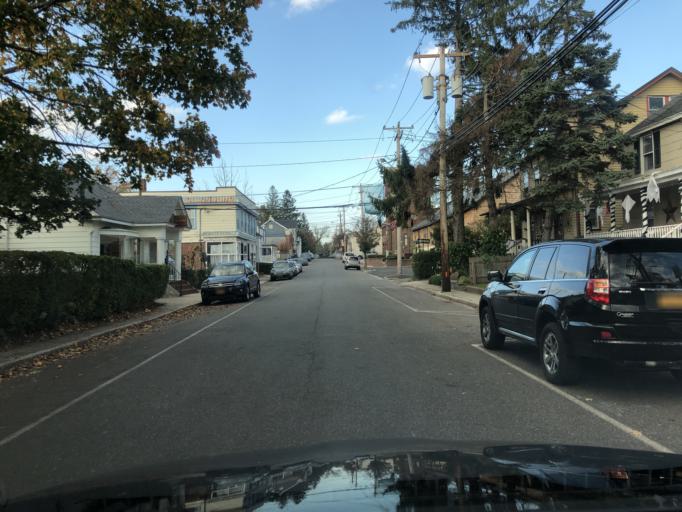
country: US
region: New York
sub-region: Nassau County
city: Sea Cliff
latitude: 40.8476
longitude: -73.6450
